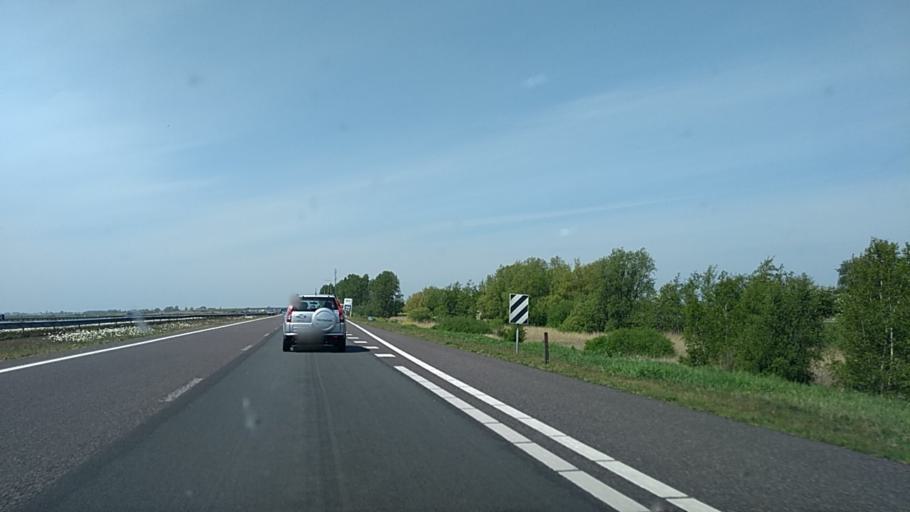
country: NL
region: Friesland
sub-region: Sudwest Fryslan
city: Oppenhuizen
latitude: 52.9821
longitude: 5.7396
